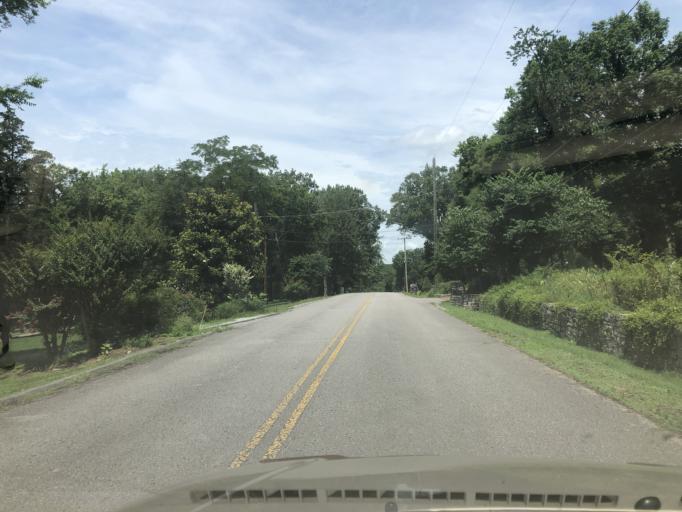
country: US
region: Tennessee
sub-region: Davidson County
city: Lakewood
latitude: 36.2454
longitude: -86.6855
